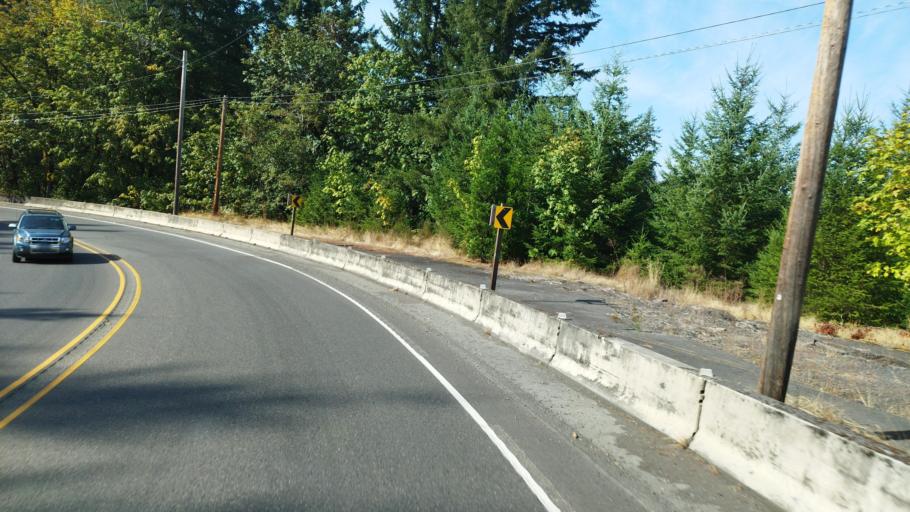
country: US
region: Oregon
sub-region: Washington County
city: Bethany
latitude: 45.6138
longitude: -122.8595
